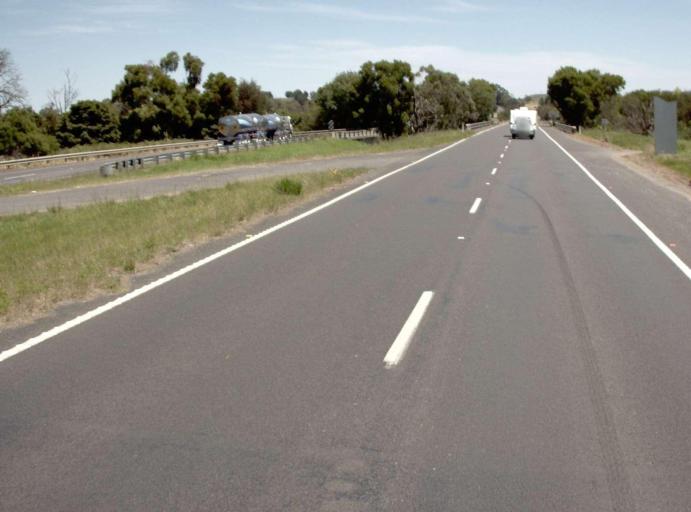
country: AU
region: Victoria
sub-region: Cardinia
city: Bunyip
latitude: -38.0830
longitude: 145.7539
